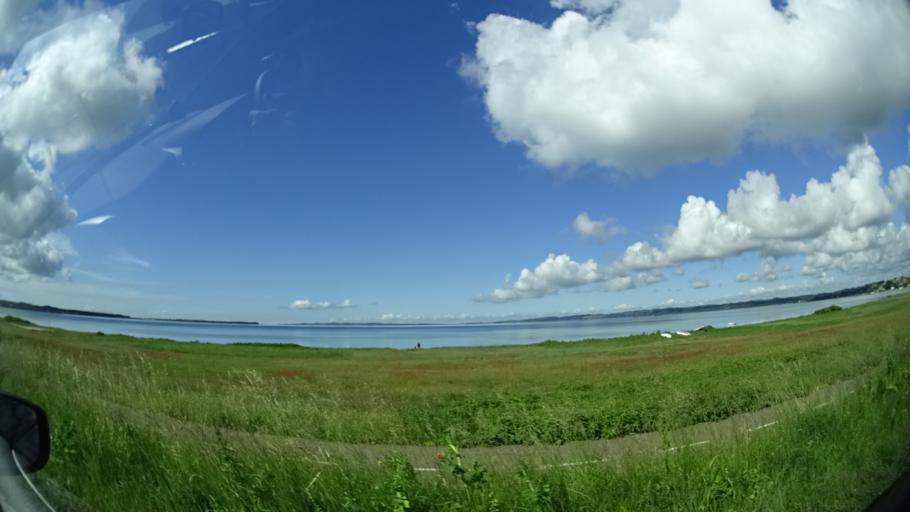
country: DK
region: Central Jutland
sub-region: Syddjurs Kommune
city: Ebeltoft
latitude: 56.2203
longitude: 10.6689
